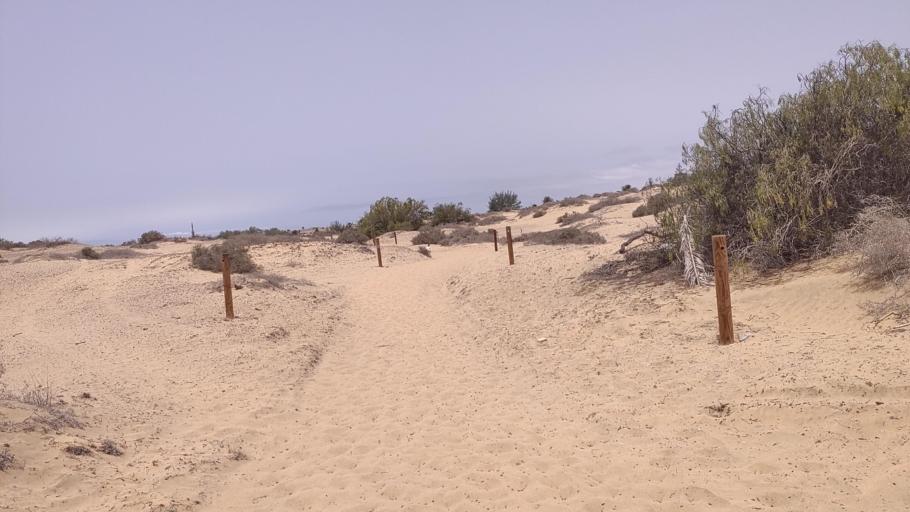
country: ES
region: Canary Islands
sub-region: Provincia de Las Palmas
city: Playa del Ingles
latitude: 27.7452
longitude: -15.5894
